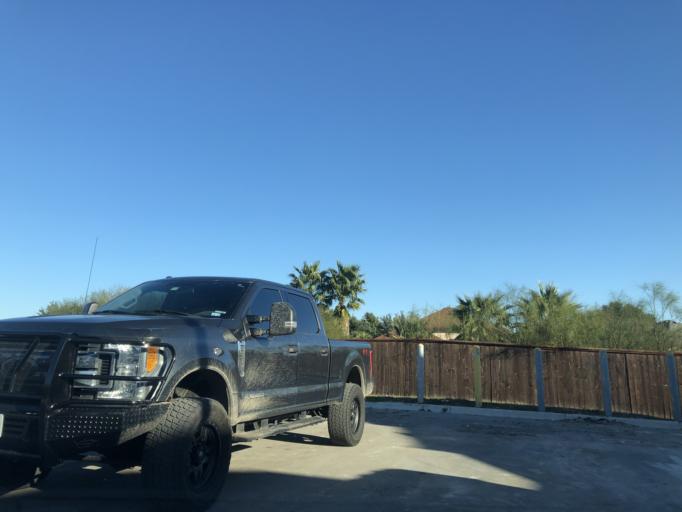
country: US
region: Texas
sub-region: Travis County
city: Windemere
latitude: 30.4713
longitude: -97.6576
